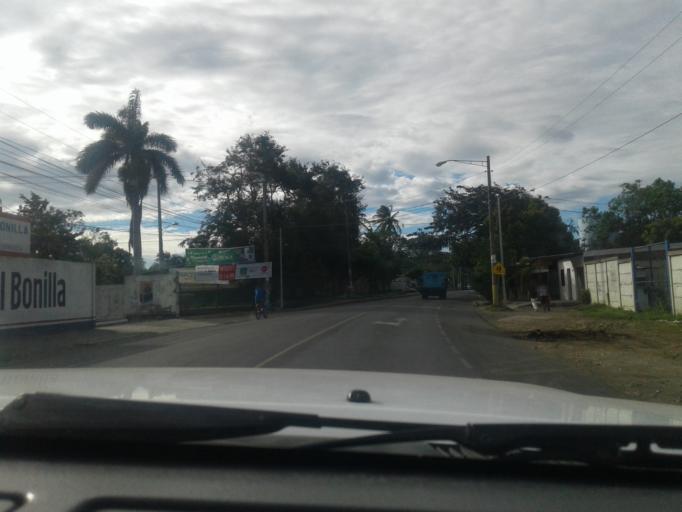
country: NI
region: Carazo
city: Jinotepe
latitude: 11.8520
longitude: -86.2043
